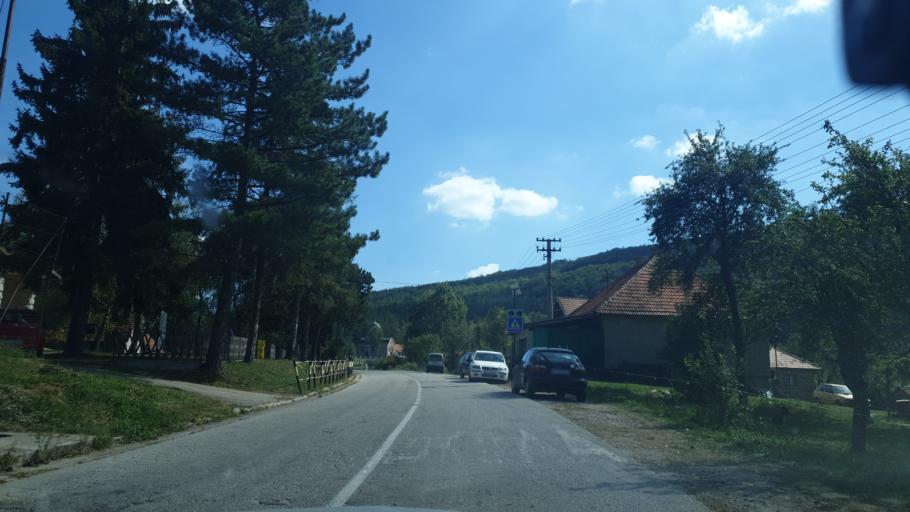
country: RS
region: Central Serbia
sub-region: Zlatiborski Okrug
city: Kosjeric
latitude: 44.0068
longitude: 20.0497
